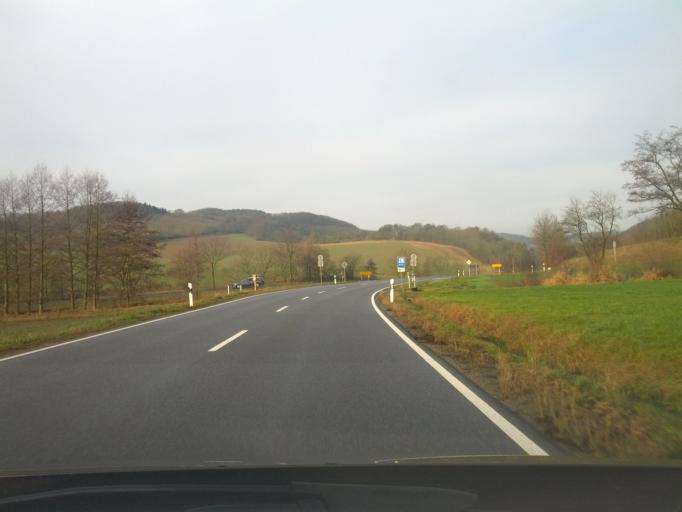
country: DE
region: Hesse
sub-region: Regierungsbezirk Kassel
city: Weissenborn
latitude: 51.1068
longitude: 10.0543
